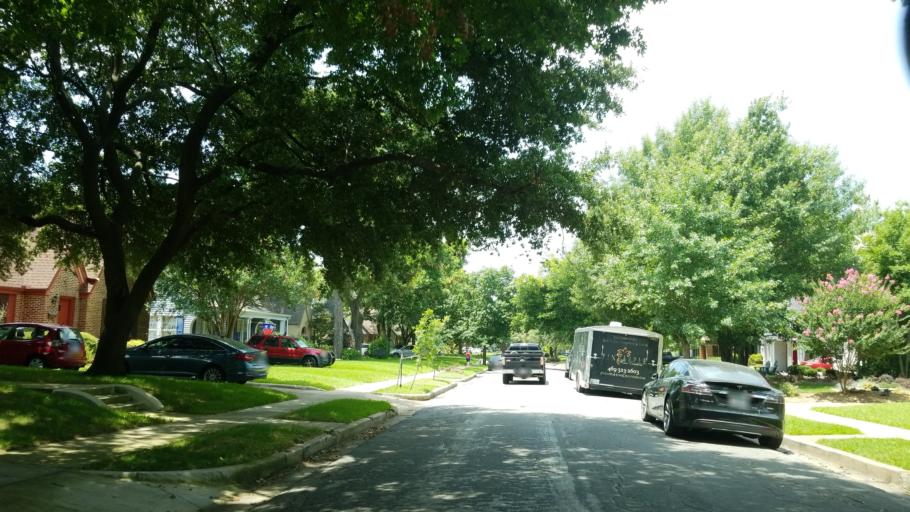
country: US
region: Texas
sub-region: Dallas County
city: Highland Park
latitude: 32.8264
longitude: -96.7786
